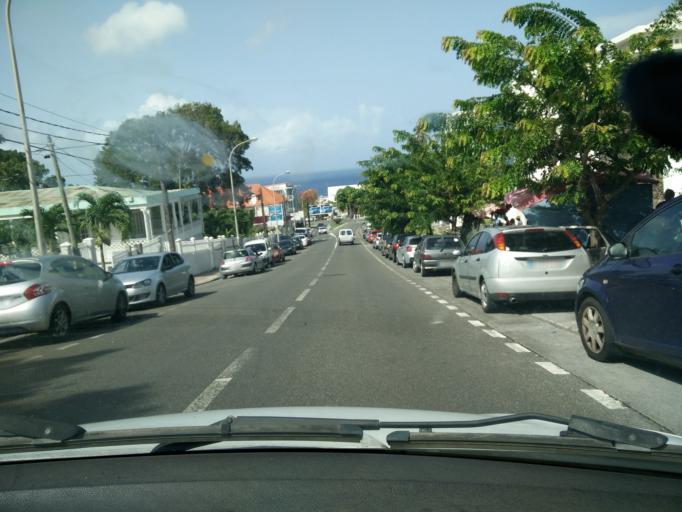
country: GP
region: Guadeloupe
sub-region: Guadeloupe
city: Basse-Terre
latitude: 15.9921
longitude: -61.7210
